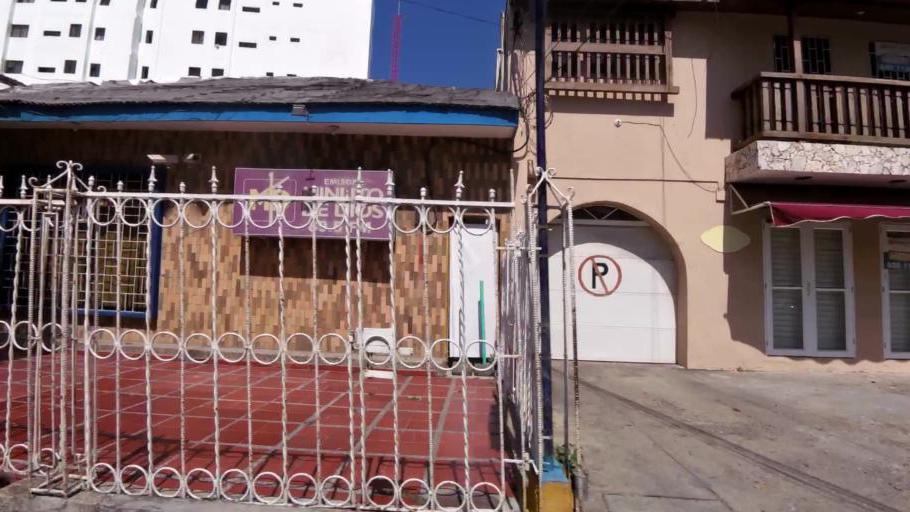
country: CO
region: Bolivar
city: Cartagena
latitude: 10.4174
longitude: -75.5317
